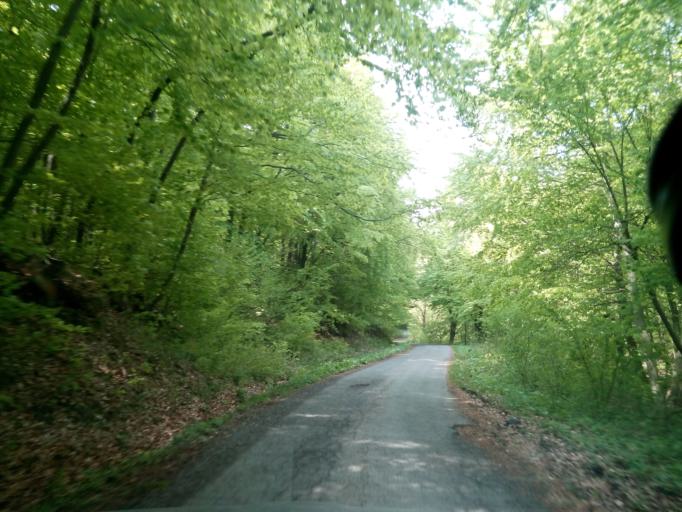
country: SK
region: Presovsky
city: Giraltovce
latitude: 48.9673
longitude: 21.4995
